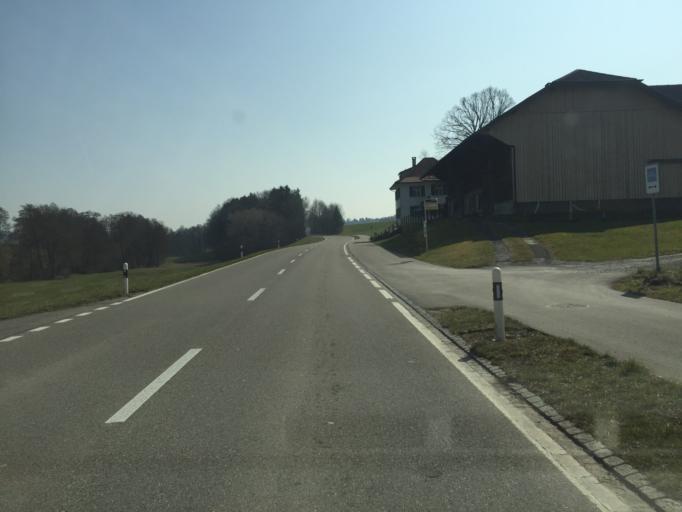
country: CH
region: Thurgau
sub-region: Frauenfeld District
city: Huttwilen
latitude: 47.5993
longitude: 8.8826
